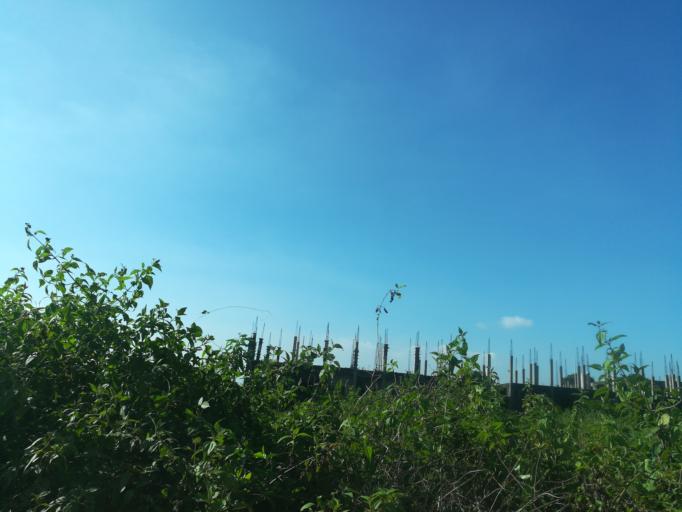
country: NG
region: Lagos
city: Ikorodu
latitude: 6.5632
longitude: 3.5346
